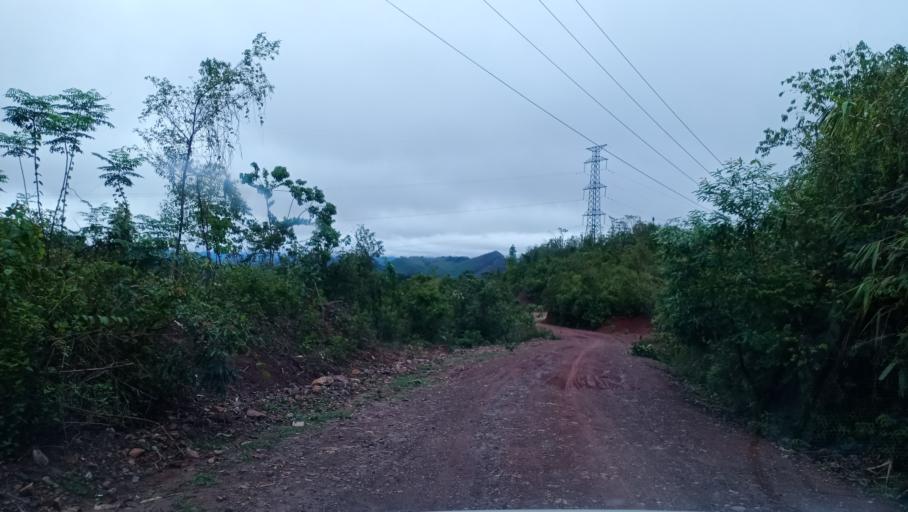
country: LA
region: Phongsali
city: Phongsali
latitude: 21.3422
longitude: 102.0753
